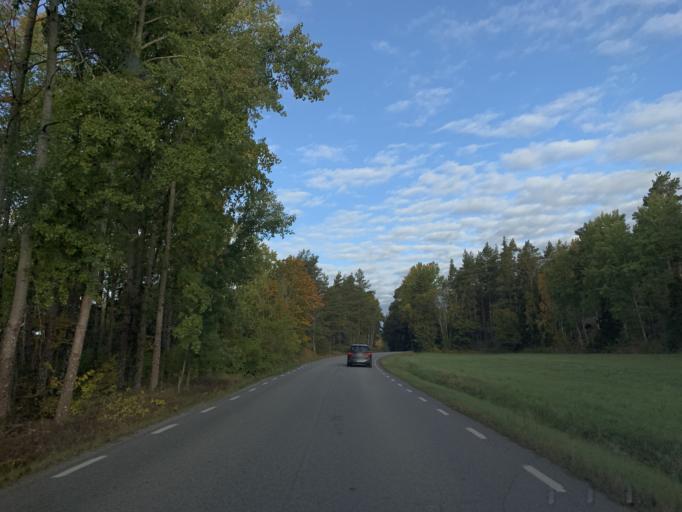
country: SE
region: Stockholm
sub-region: Upplands-Bro Kommun
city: Bro
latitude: 59.5049
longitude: 17.6079
